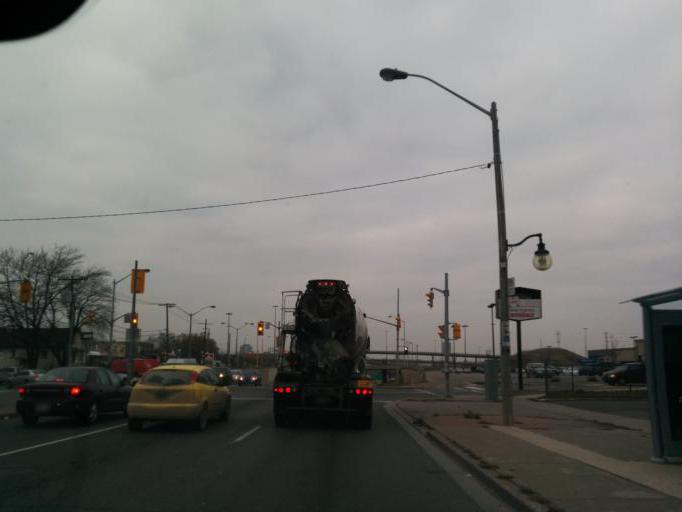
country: CA
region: Ontario
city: Etobicoke
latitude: 43.6087
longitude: -79.5481
